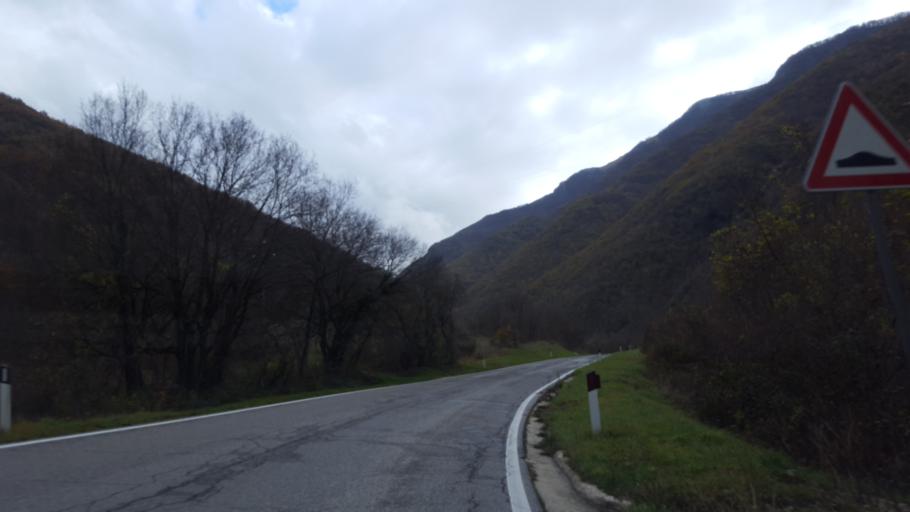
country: IT
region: The Marches
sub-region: Provincia di Macerata
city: Fluminata
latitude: 42.9126
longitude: 13.1284
